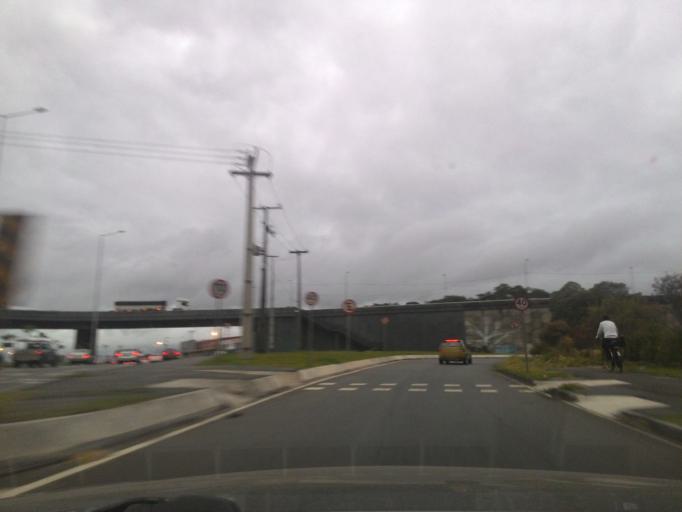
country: BR
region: Parana
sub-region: Pinhais
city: Pinhais
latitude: -25.4447
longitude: -49.2341
